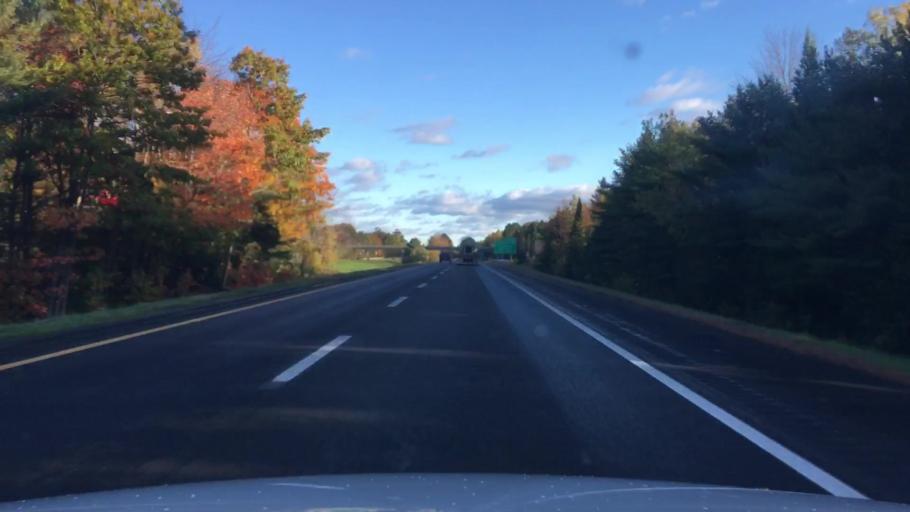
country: US
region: Maine
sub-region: Penobscot County
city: Orono
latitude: 44.8857
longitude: -68.6947
